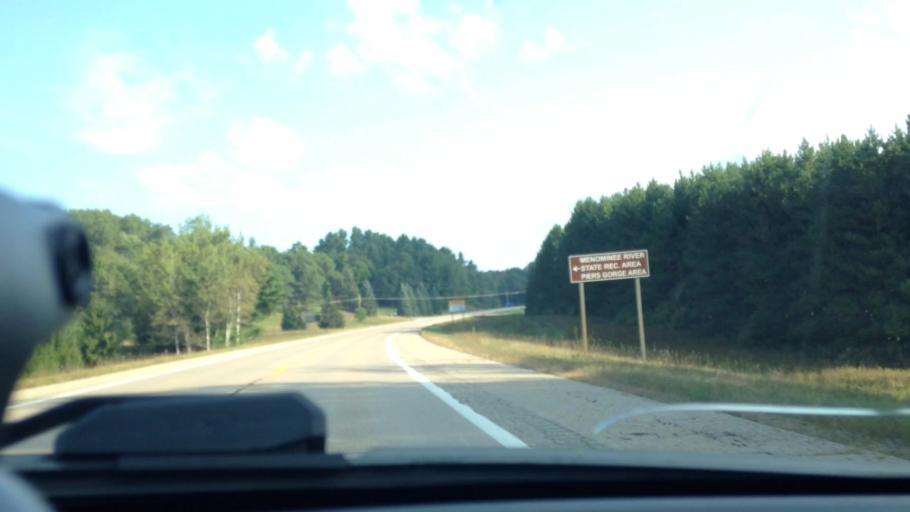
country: US
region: Michigan
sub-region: Dickinson County
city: Norway
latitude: 45.7594
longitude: -87.9215
